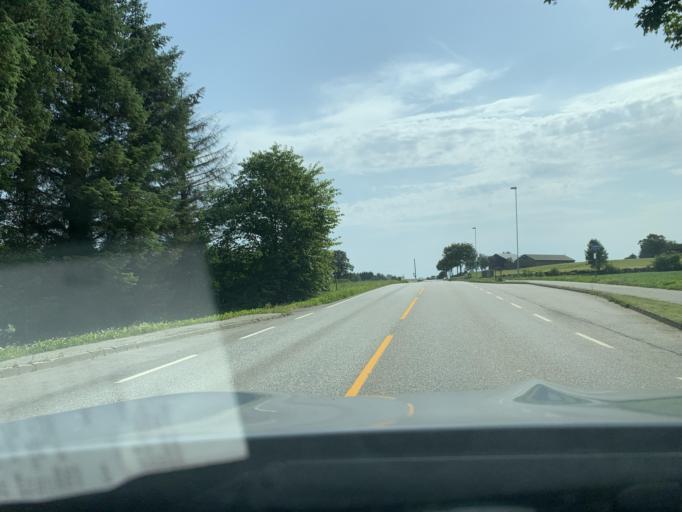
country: NO
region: Rogaland
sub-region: Klepp
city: Kleppe
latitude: 58.7657
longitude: 5.6271
